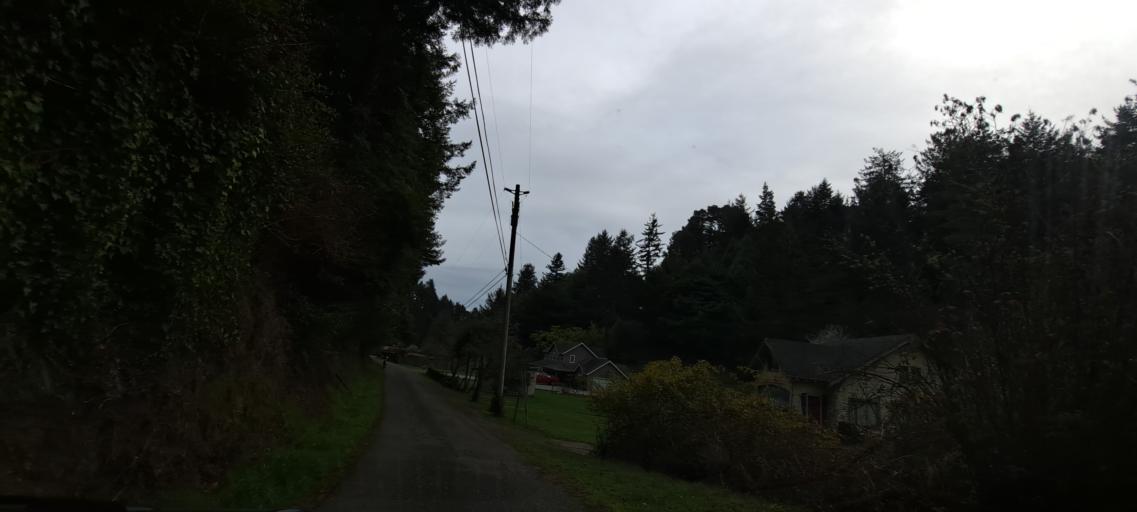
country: US
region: California
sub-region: Humboldt County
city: Fortuna
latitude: 40.6058
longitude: -124.1588
